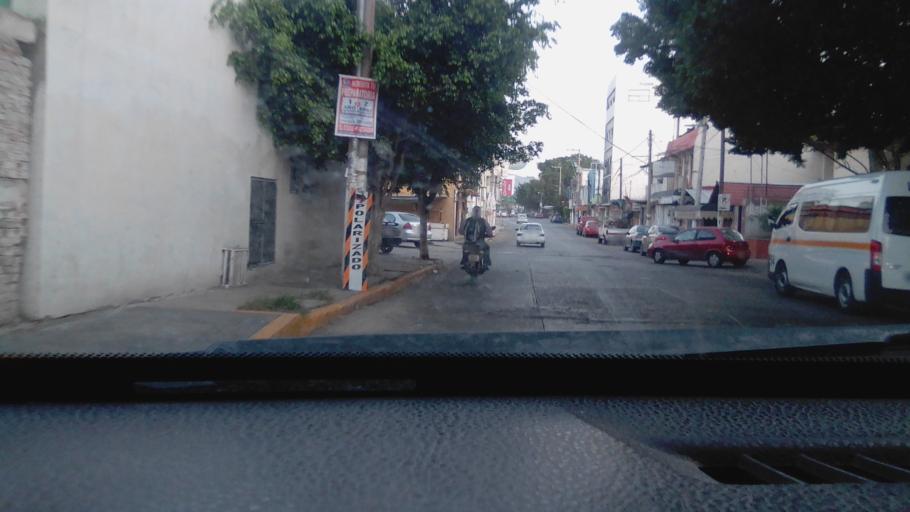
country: MX
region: Guerrero
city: Chilpancingo de los Bravos
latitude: 17.5587
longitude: -99.5053
